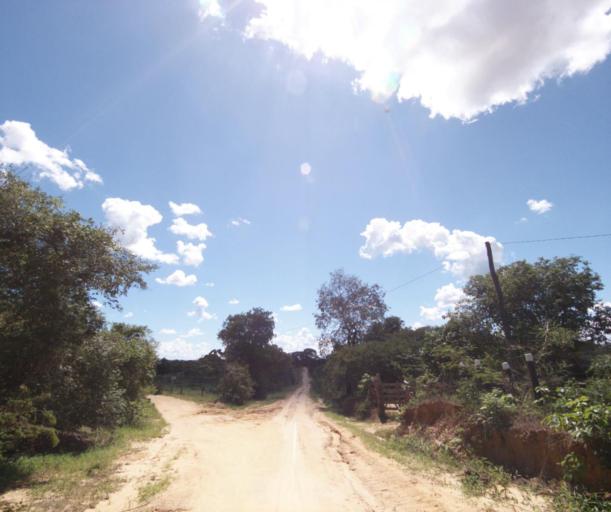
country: BR
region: Bahia
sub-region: Carinhanha
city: Carinhanha
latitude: -14.2343
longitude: -44.3126
